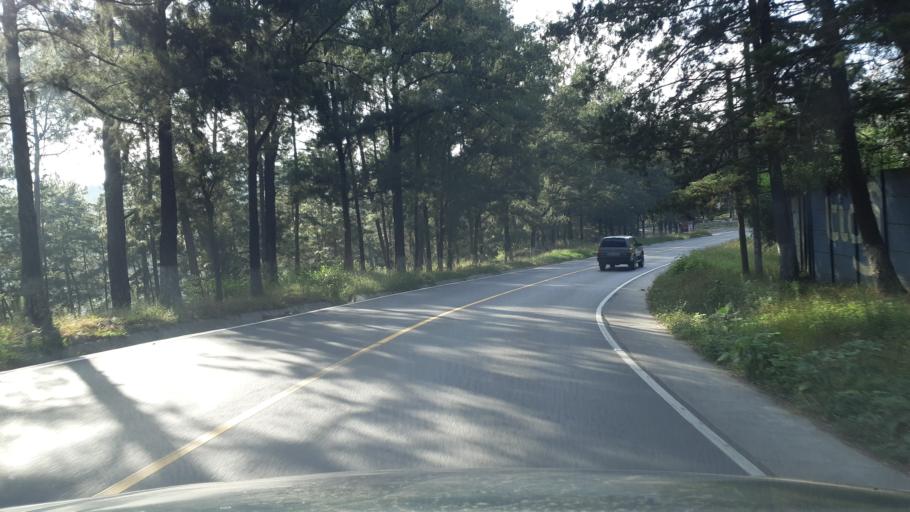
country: GT
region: Chimaltenango
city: El Tejar
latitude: 14.6376
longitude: -90.8121
